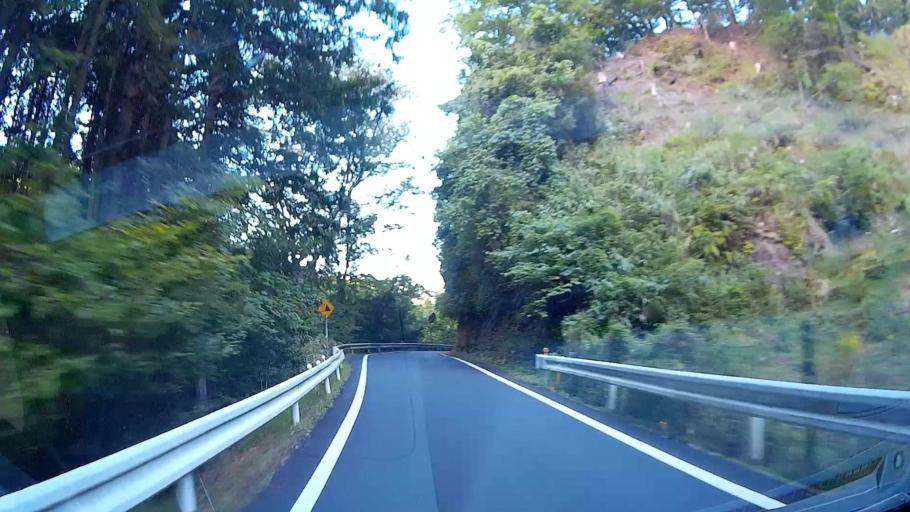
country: JP
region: Shizuoka
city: Shizuoka-shi
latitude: 35.1372
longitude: 138.2693
